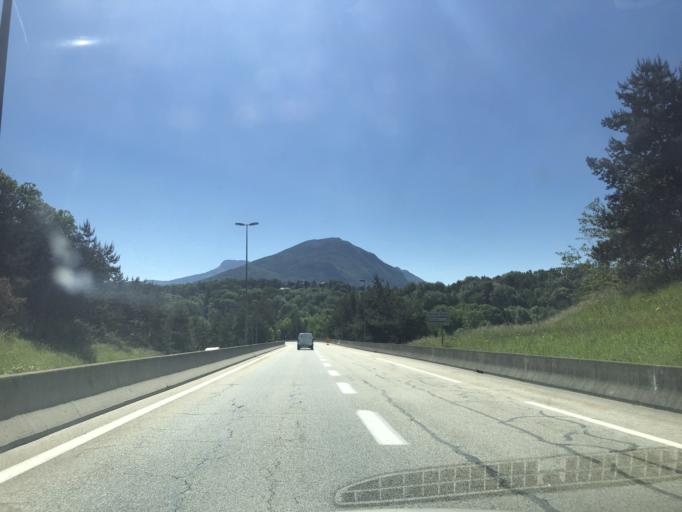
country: FR
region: Rhone-Alpes
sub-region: Departement de la Haute-Savoie
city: Pringy
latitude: 45.9362
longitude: 6.1299
